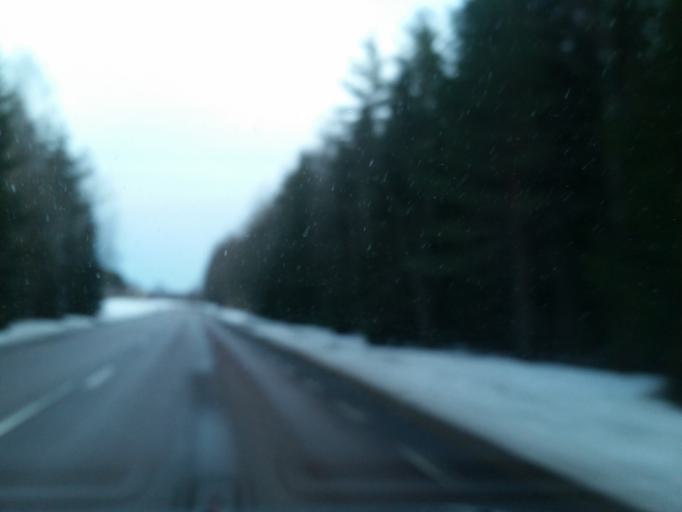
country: SE
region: Gaevleborg
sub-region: Sandvikens Kommun
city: Sandviken
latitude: 60.6640
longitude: 16.6971
